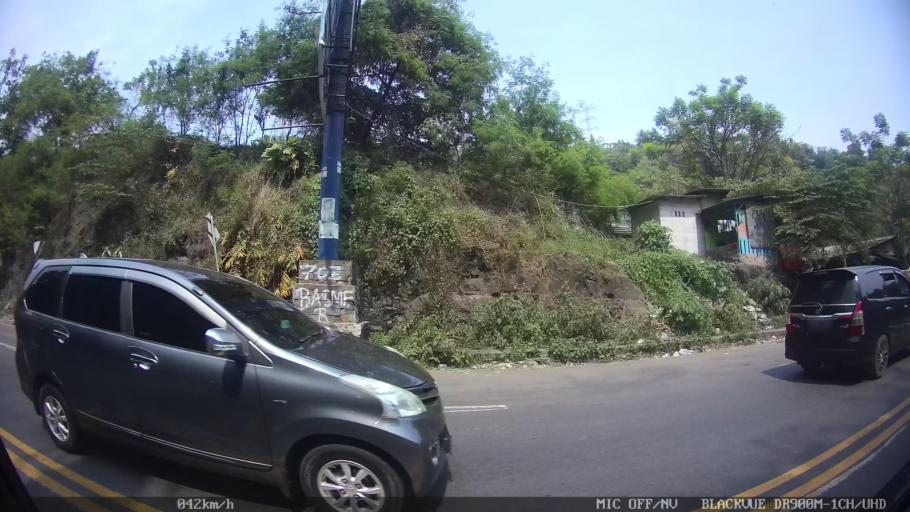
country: ID
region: Banten
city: Curug
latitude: -5.9455
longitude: 106.0044
